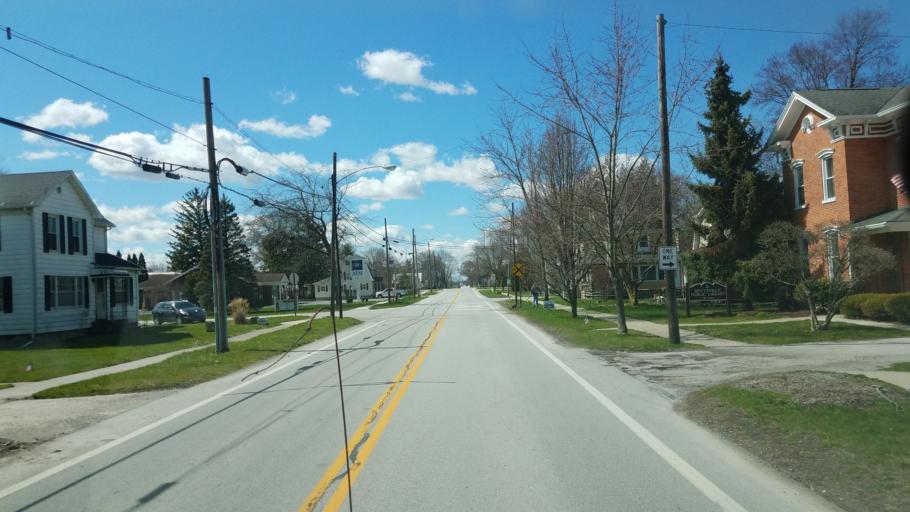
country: US
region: Ohio
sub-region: Sandusky County
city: Ballville
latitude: 41.2460
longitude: -83.2351
